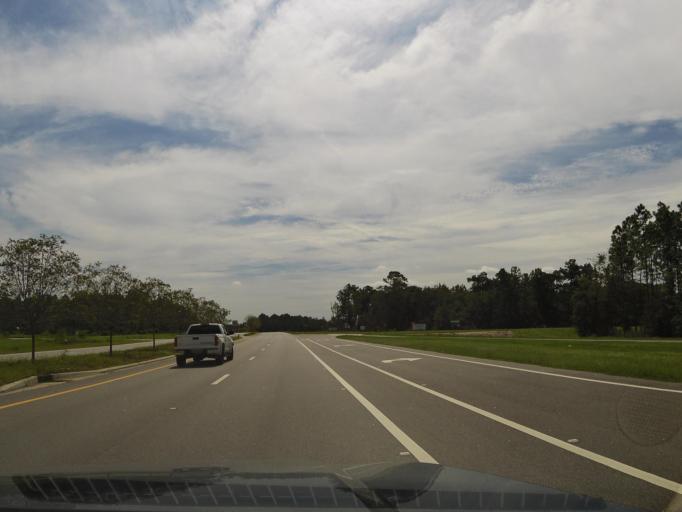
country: US
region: Florida
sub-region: Saint Johns County
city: Fruit Cove
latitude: 30.0284
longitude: -81.5247
